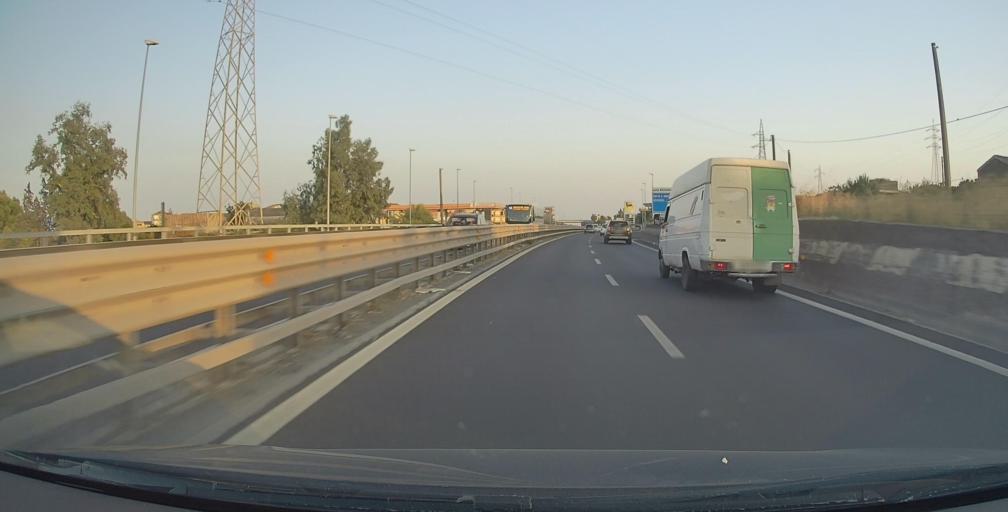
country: IT
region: Sicily
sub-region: Catania
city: Belvedere-Piano Tavola
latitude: 37.5265
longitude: 14.9944
